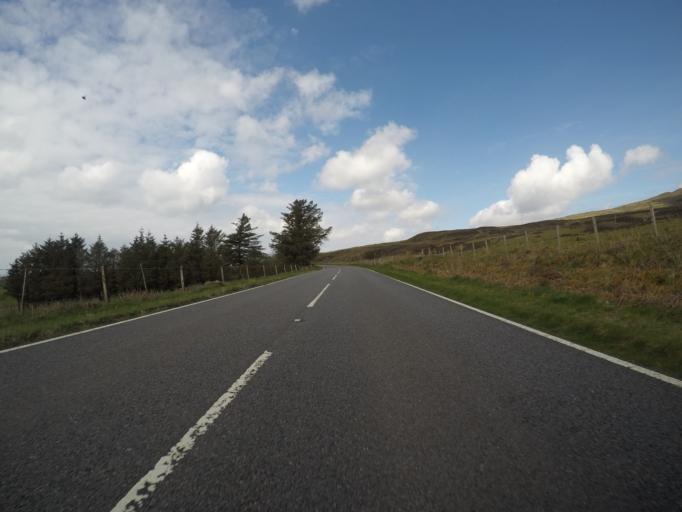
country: GB
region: Scotland
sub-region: Highland
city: Portree
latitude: 57.5586
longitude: -6.3635
